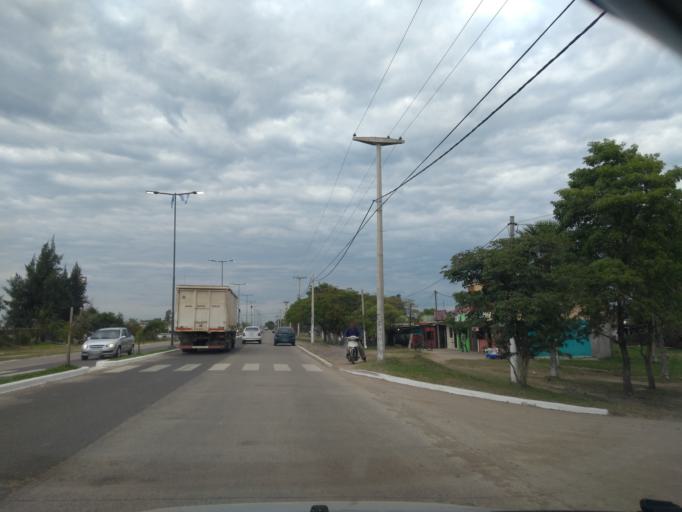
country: AR
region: Chaco
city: Puerto Vilelas
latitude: -27.5137
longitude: -58.9420
